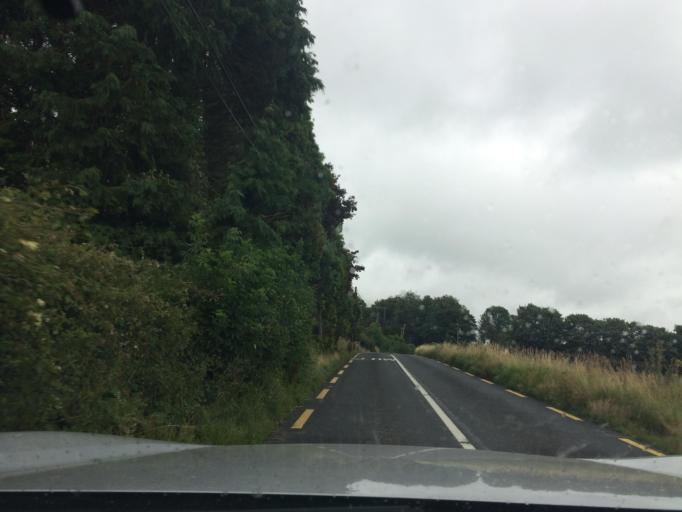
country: IE
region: Munster
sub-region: South Tipperary
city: Cluain Meala
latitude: 52.2914
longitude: -7.7628
